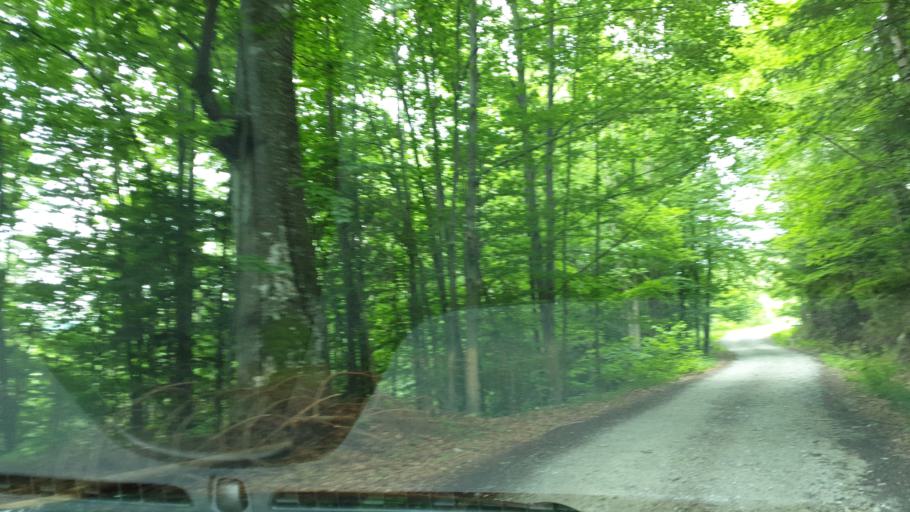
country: RO
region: Hunedoara
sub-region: Comuna Uricani
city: Uricani
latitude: 45.3066
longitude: 22.9849
